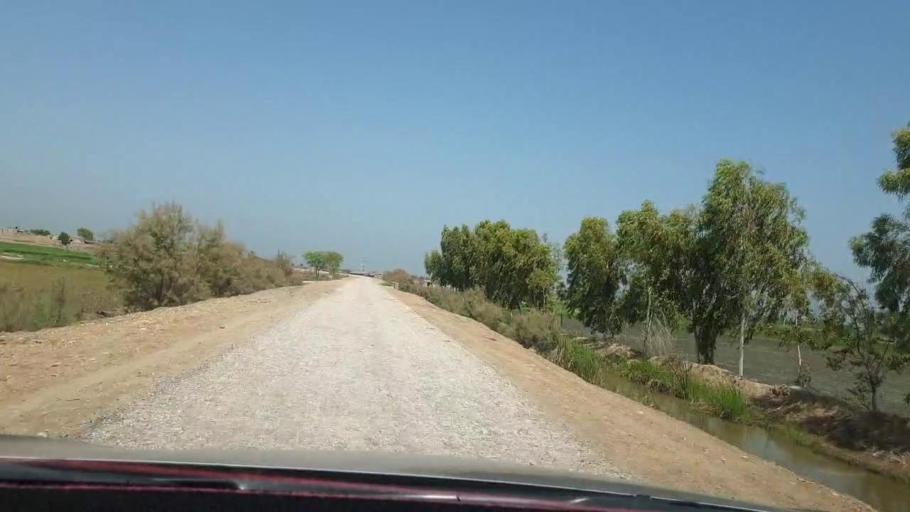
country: PK
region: Sindh
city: Warah
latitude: 27.5395
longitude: 67.7421
